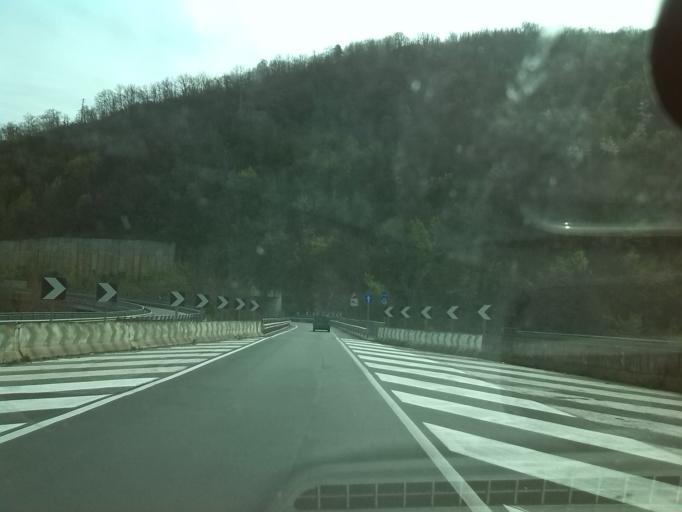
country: IT
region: Liguria
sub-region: Provincia di Imperia
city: Pieve di Teco
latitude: 44.0368
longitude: 7.9276
